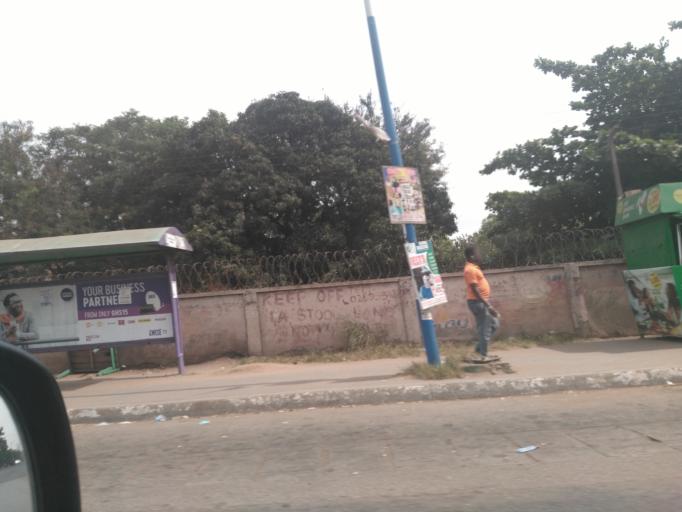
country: GH
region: Greater Accra
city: Accra
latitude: 5.5901
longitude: -0.1825
